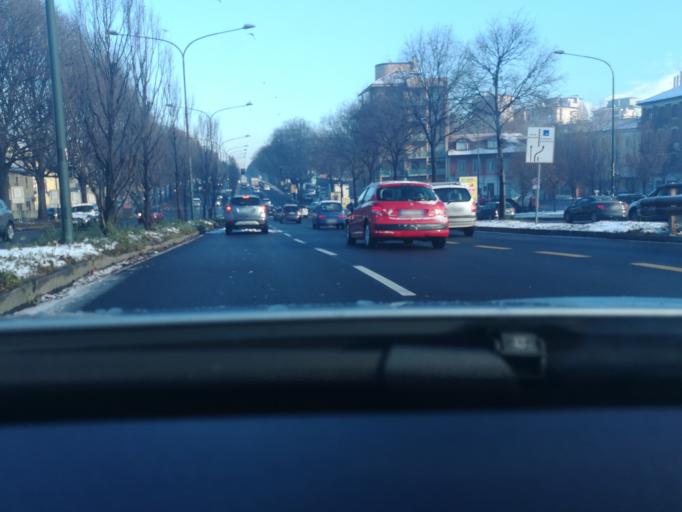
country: IT
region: Piedmont
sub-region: Provincia di Torino
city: Turin
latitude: 45.0909
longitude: 7.6540
